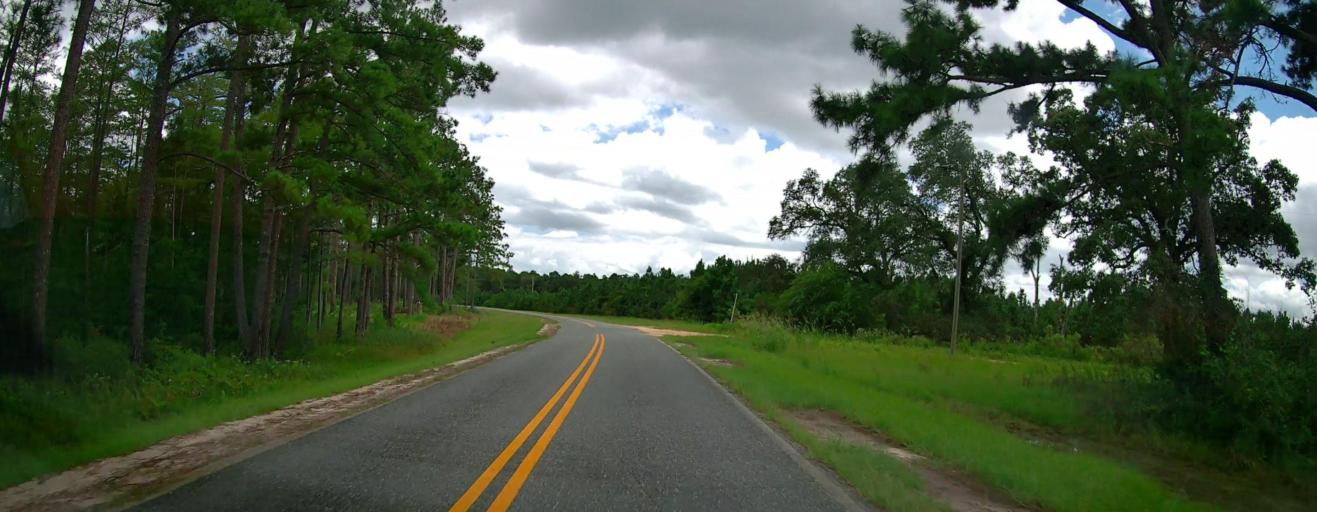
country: US
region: Georgia
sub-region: Turner County
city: Ashburn
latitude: 31.7064
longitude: -83.5053
